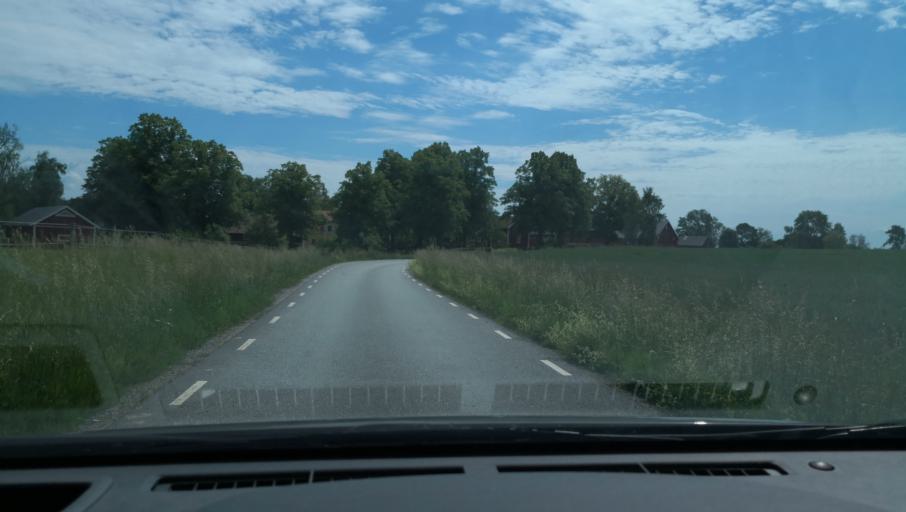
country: SE
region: Uppsala
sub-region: Habo Kommun
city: Balsta
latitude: 59.6976
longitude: 17.4799
